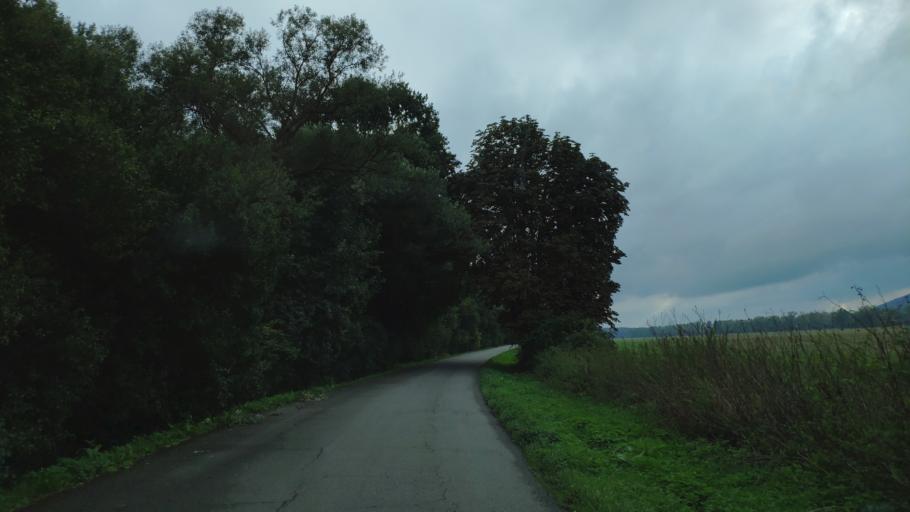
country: SK
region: Kosicky
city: Moldava nad Bodvou
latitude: 48.5891
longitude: 20.8990
